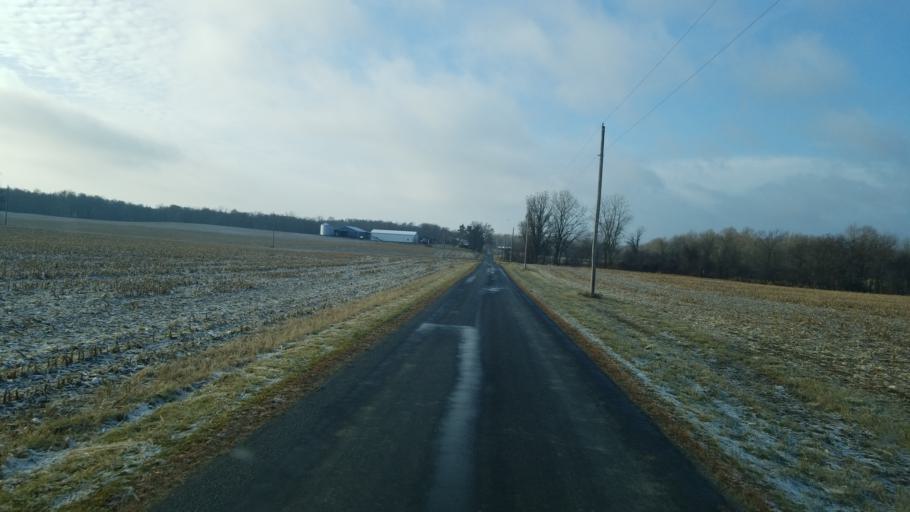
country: US
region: Ohio
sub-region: Crawford County
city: Crestline
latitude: 40.8743
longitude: -82.8000
